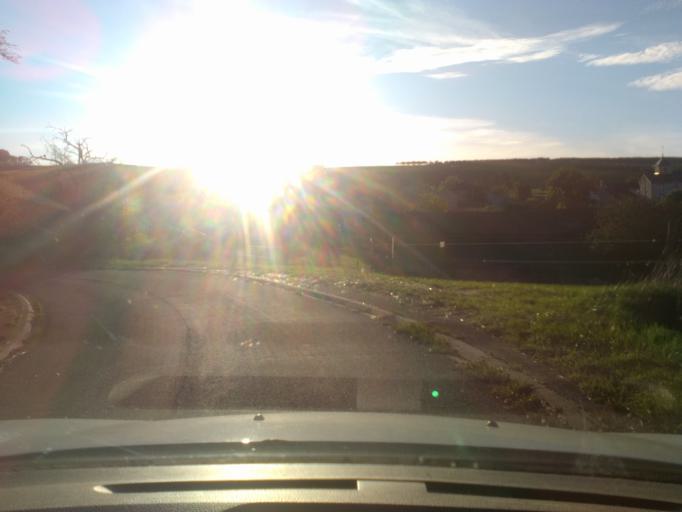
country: FR
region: Lorraine
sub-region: Departement des Vosges
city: Vincey
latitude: 48.3245
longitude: 6.3012
